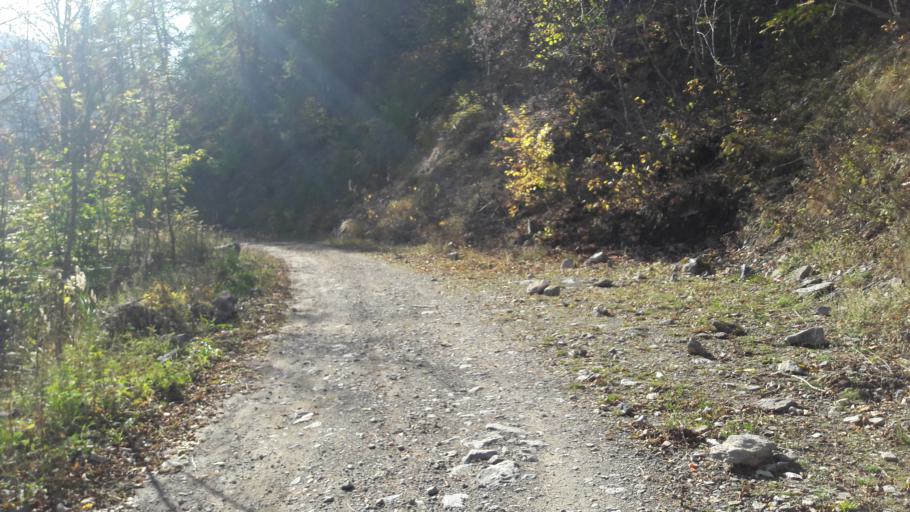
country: FR
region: Rhone-Alpes
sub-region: Departement de la Savoie
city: Valloire
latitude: 45.1931
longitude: 6.4282
